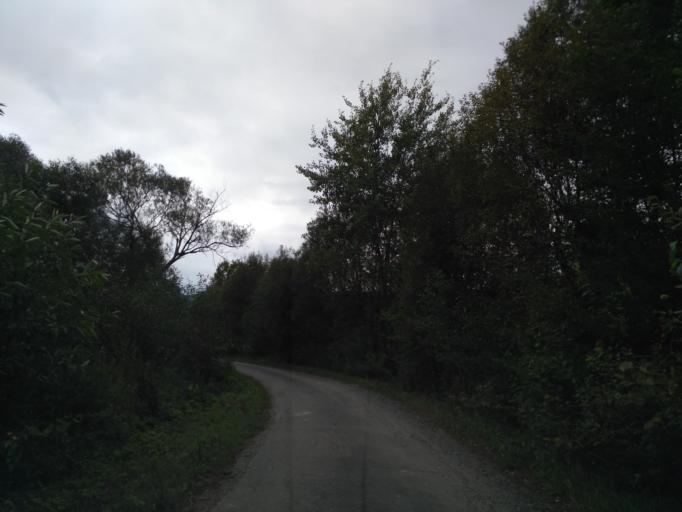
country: SK
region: Presovsky
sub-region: Okres Presov
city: Presov
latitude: 48.9152
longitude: 21.1803
